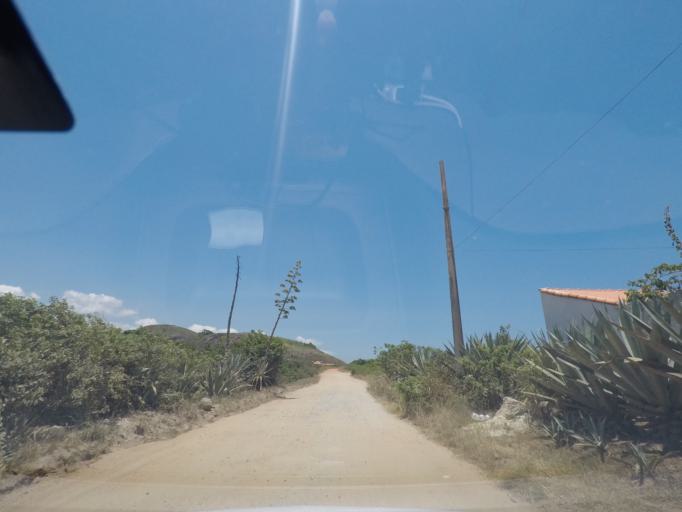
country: BR
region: Rio de Janeiro
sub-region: Niteroi
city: Niteroi
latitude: -22.9689
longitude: -43.0069
